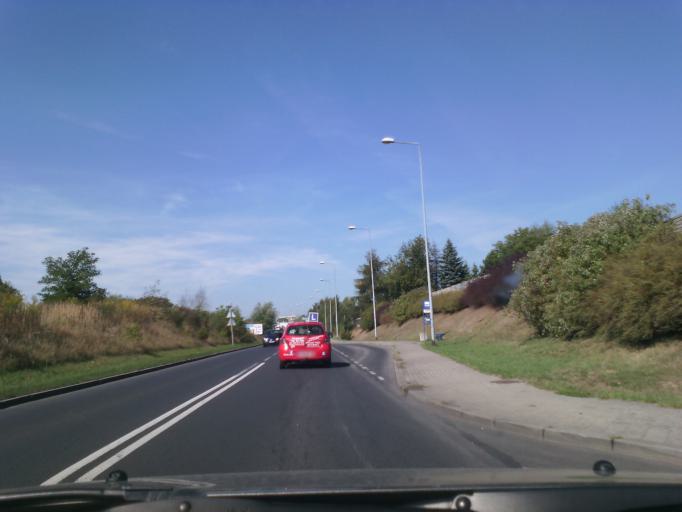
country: PL
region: Silesian Voivodeship
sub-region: Rybnik
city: Rybnik
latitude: 50.0876
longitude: 18.5244
